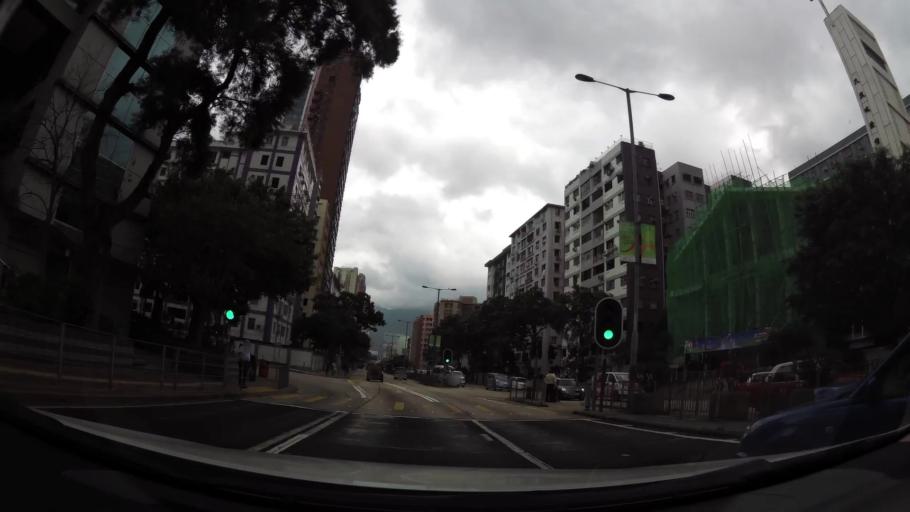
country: HK
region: Kowloon City
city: Kowloon
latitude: 22.3249
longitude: 114.1855
